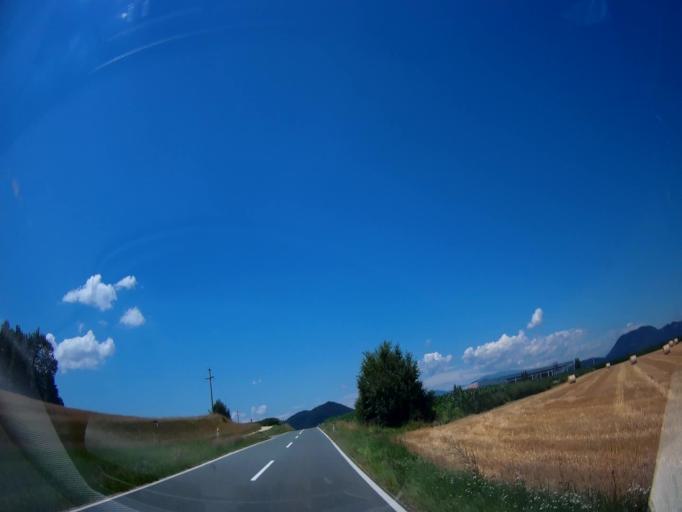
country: AT
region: Carinthia
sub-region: Politischer Bezirk Volkermarkt
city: Bleiburg/Pliberk
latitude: 46.5998
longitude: 14.7913
